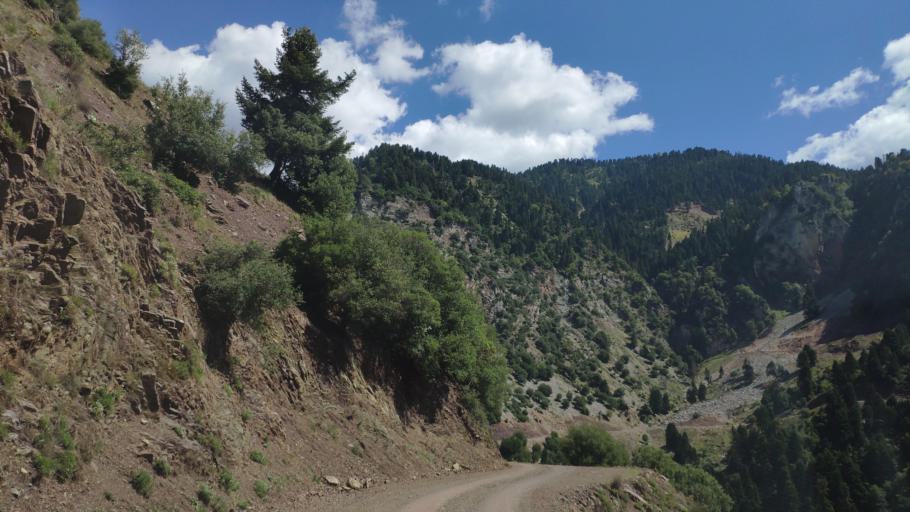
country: GR
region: Central Greece
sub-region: Nomos Evrytanias
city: Kerasochori
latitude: 39.1395
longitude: 21.6541
